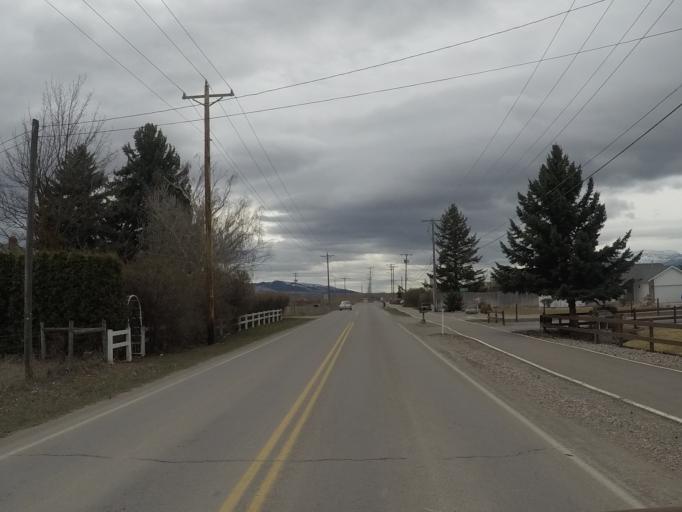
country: US
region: Montana
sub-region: Missoula County
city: Orchard Homes
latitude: 46.8896
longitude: -114.0553
